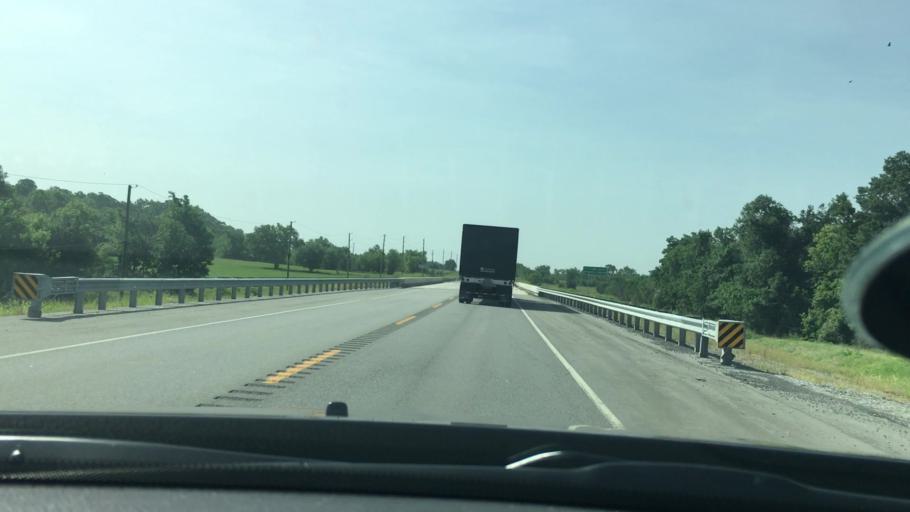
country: US
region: Oklahoma
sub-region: Coal County
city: Coalgate
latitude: 34.4465
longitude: -96.2073
